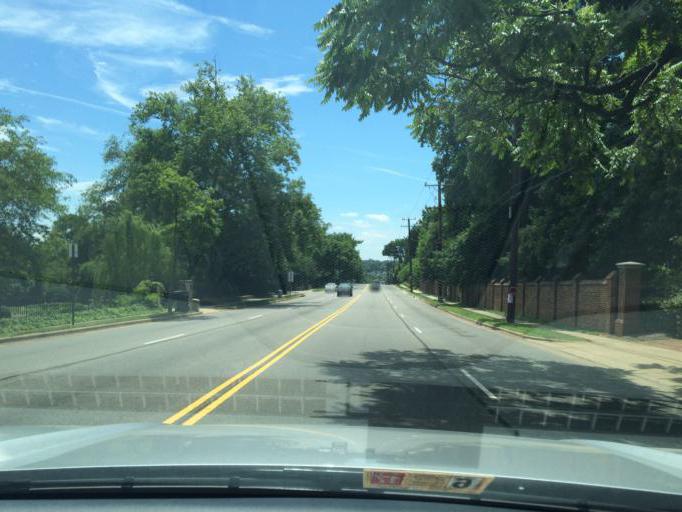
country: US
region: Virginia
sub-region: Fairfax County
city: Huntington
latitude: 38.8130
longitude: -77.0891
